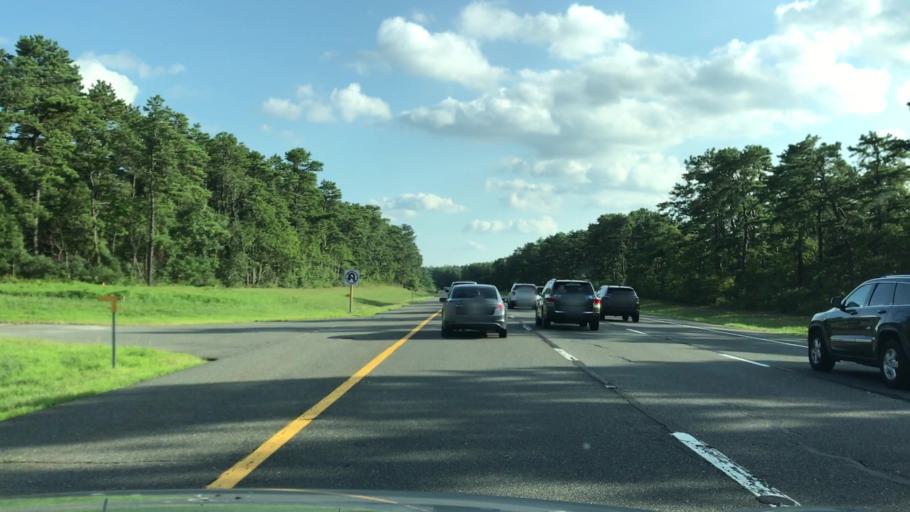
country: US
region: New Jersey
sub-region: Ocean County
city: Waretown
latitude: 39.8079
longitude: -74.2330
